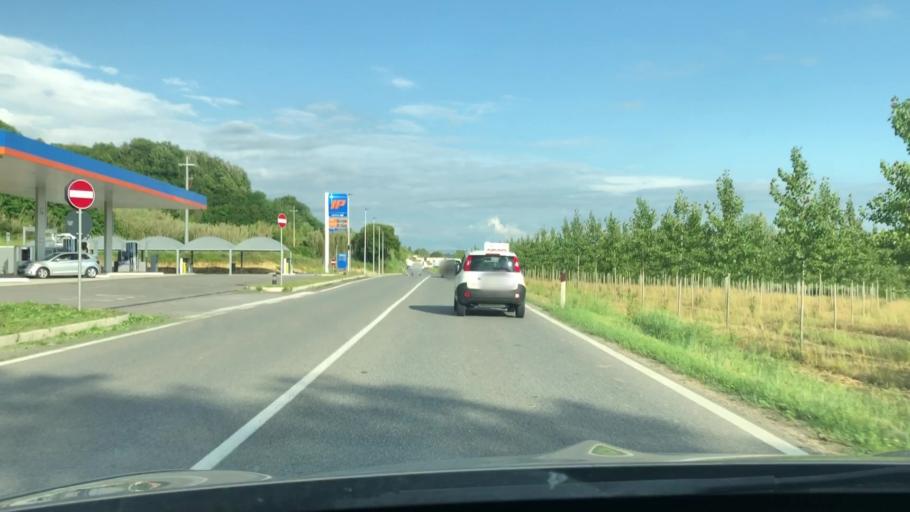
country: IT
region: Tuscany
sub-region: Province of Pisa
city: Treggiaia
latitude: 43.6132
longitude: 10.6826
